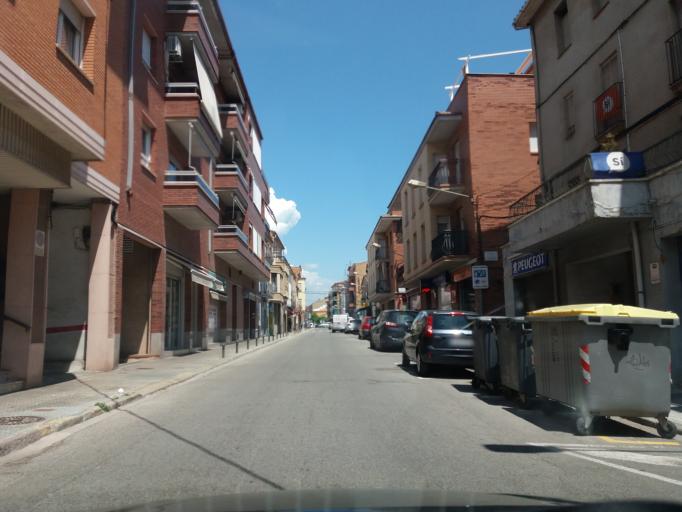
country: ES
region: Catalonia
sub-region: Provincia de Barcelona
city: Sant Joan de Vilatorrada
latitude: 41.7414
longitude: 1.8046
